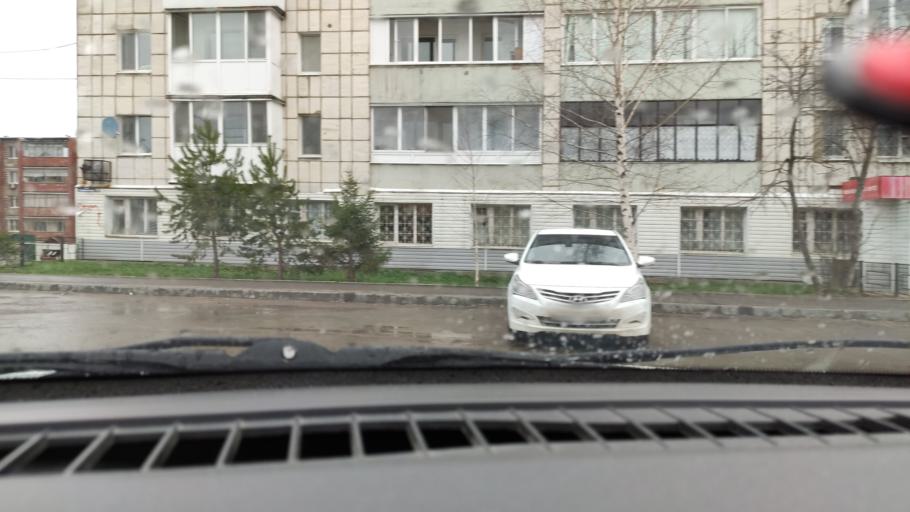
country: RU
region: Perm
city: Perm
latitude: 58.1066
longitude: 56.2970
